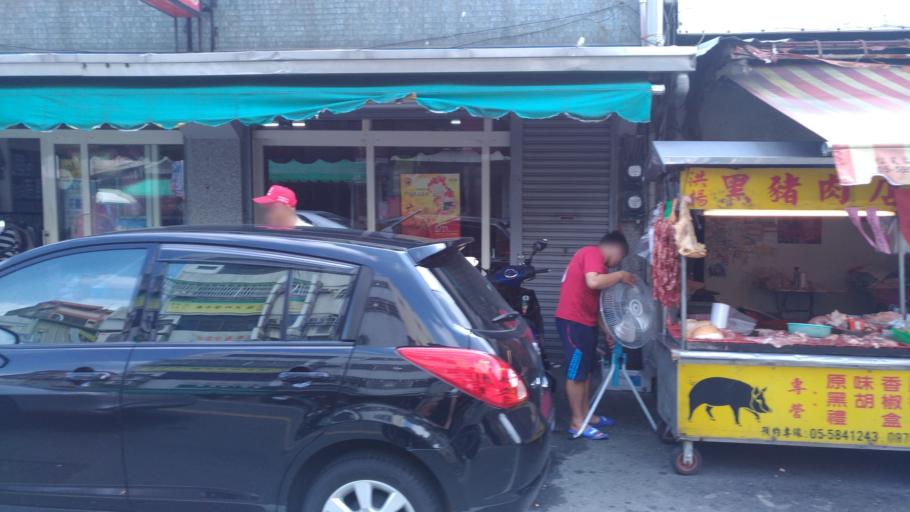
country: TW
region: Taiwan
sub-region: Yunlin
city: Douliu
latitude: 23.7571
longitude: 120.5001
